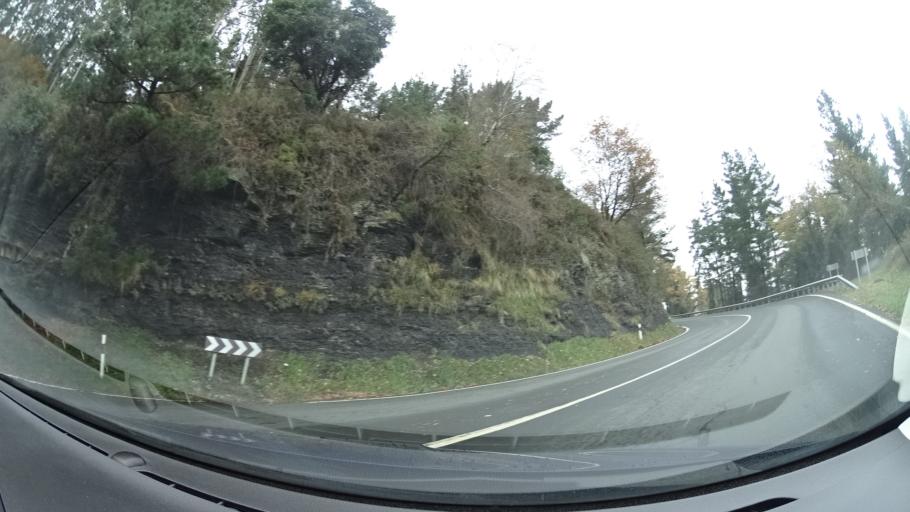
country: ES
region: Basque Country
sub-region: Bizkaia
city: Bermeo
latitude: 43.4060
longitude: -2.7567
